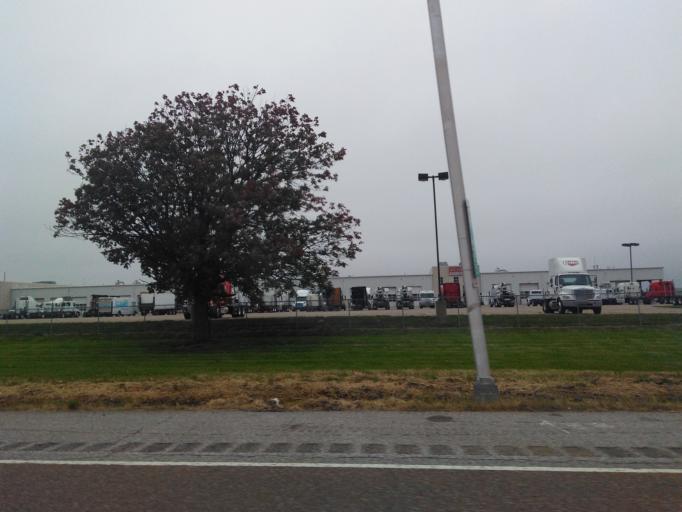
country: US
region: Illinois
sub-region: Madison County
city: Troy
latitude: 38.7414
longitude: -89.9103
